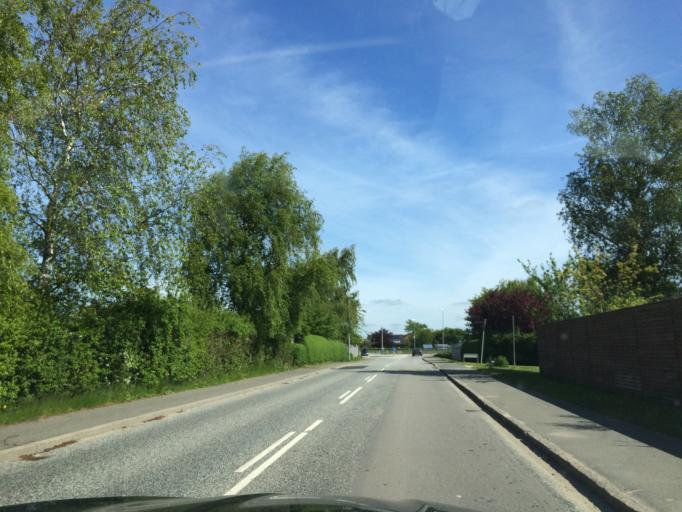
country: DK
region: Central Jutland
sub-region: Arhus Kommune
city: Hjortshoj
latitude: 56.2189
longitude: 10.2671
